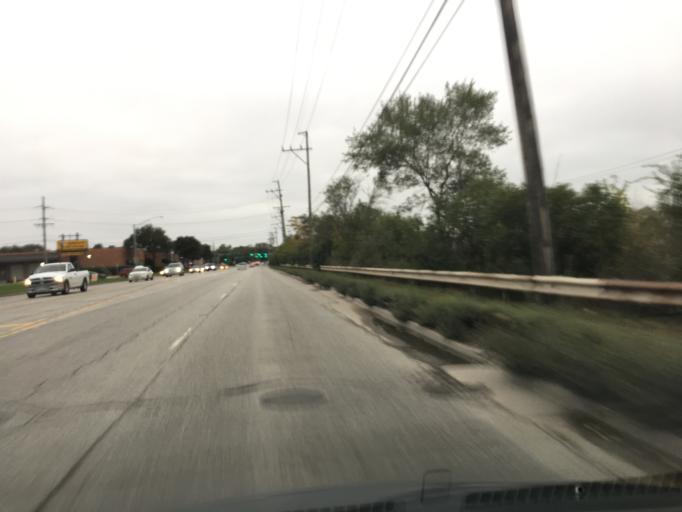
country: US
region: Illinois
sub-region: Cook County
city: Lyons
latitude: 41.8119
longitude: -87.8339
